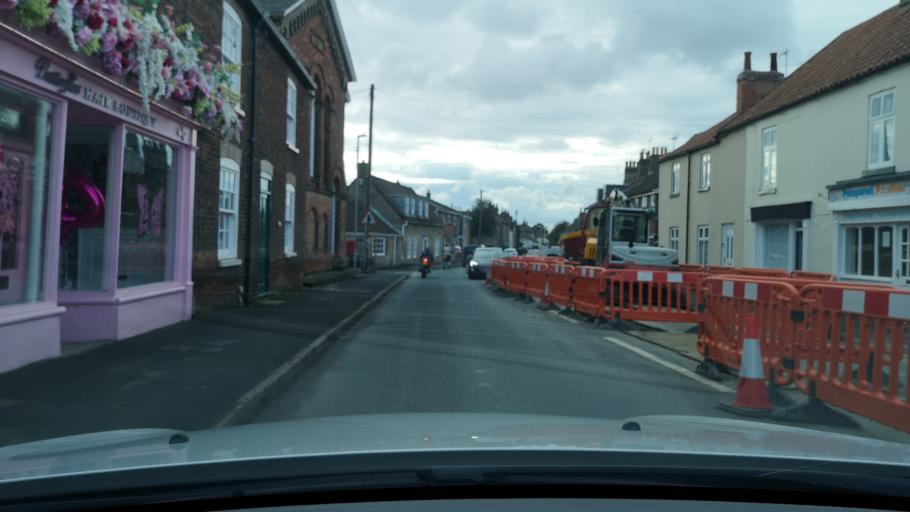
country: GB
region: England
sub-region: East Riding of Yorkshire
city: North Cave
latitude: 53.7799
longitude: -0.6468
